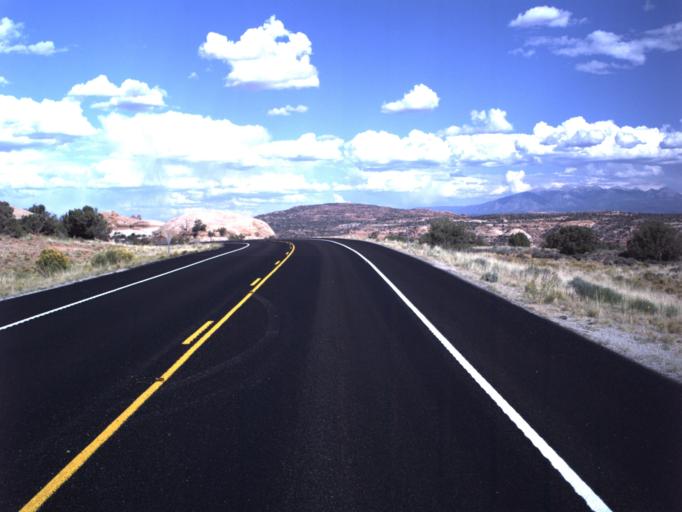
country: US
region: Utah
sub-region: Grand County
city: Moab
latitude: 38.6370
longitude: -109.7550
